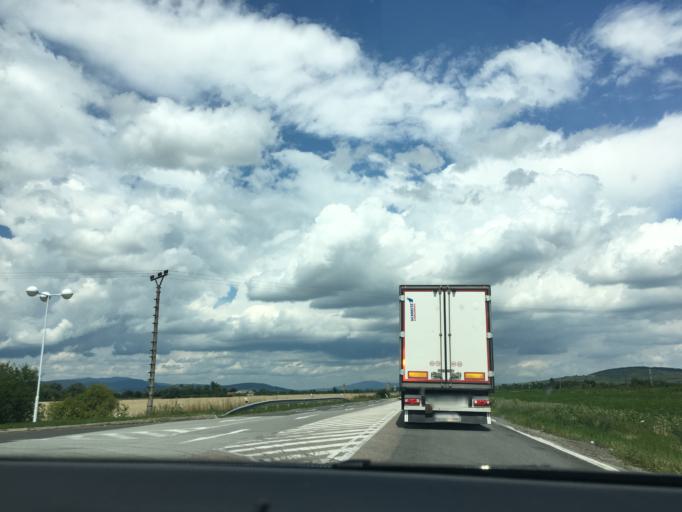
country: HU
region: Borsod-Abauj-Zemplen
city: Satoraljaujhely
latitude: 48.4283
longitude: 21.6597
